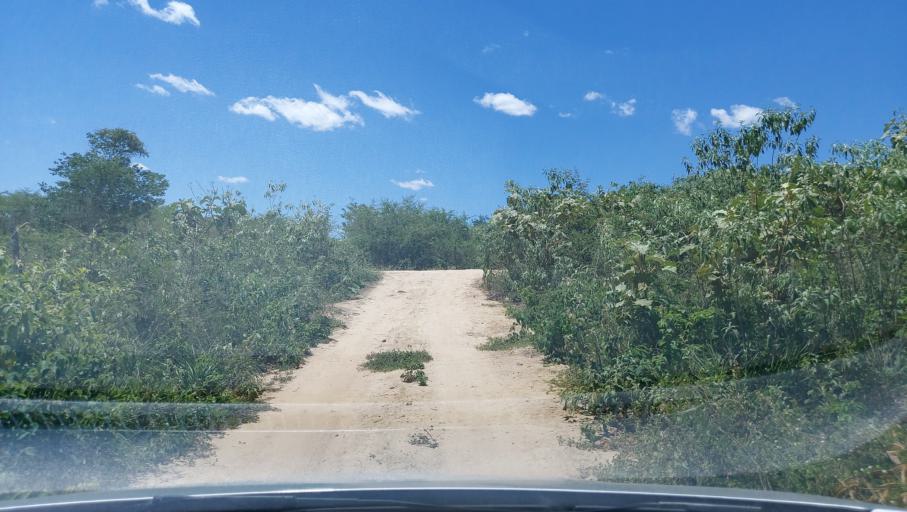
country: BR
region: Bahia
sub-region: Oliveira Dos Brejinhos
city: Beira Rio
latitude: -12.0080
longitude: -42.6305
